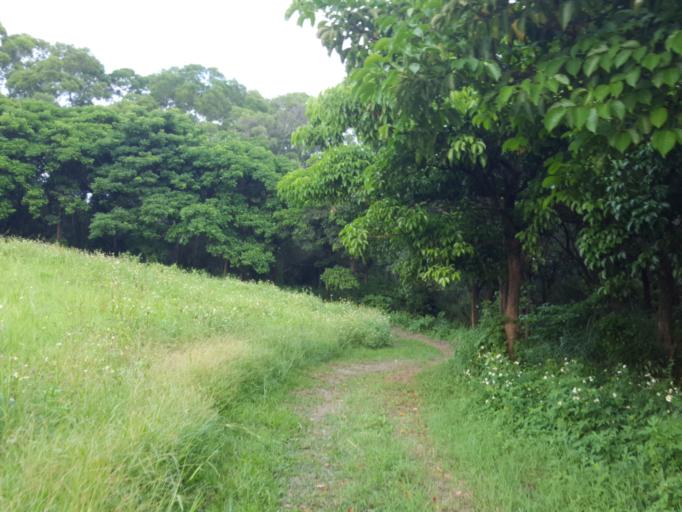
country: TW
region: Taiwan
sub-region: Hsinchu
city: Hsinchu
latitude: 24.7748
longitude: 120.9282
